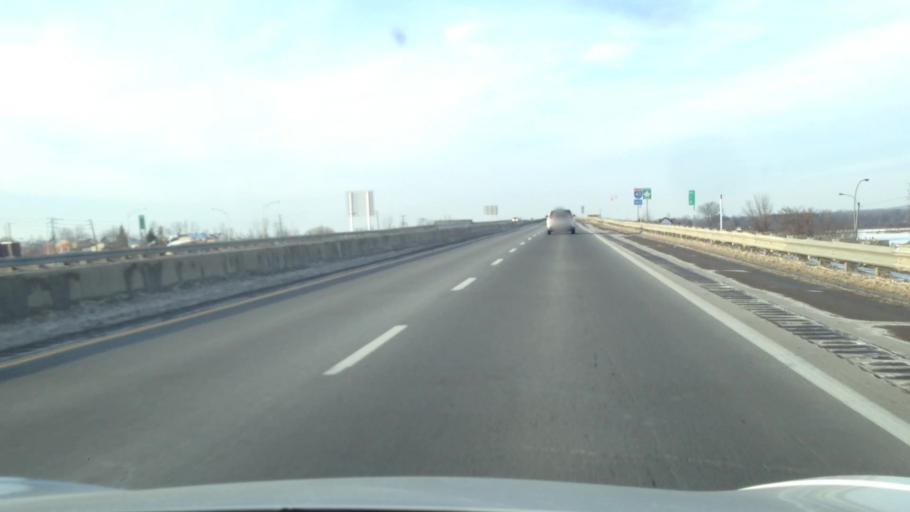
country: CA
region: Quebec
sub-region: Monteregie
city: Rigaud
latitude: 45.4786
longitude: -74.2837
